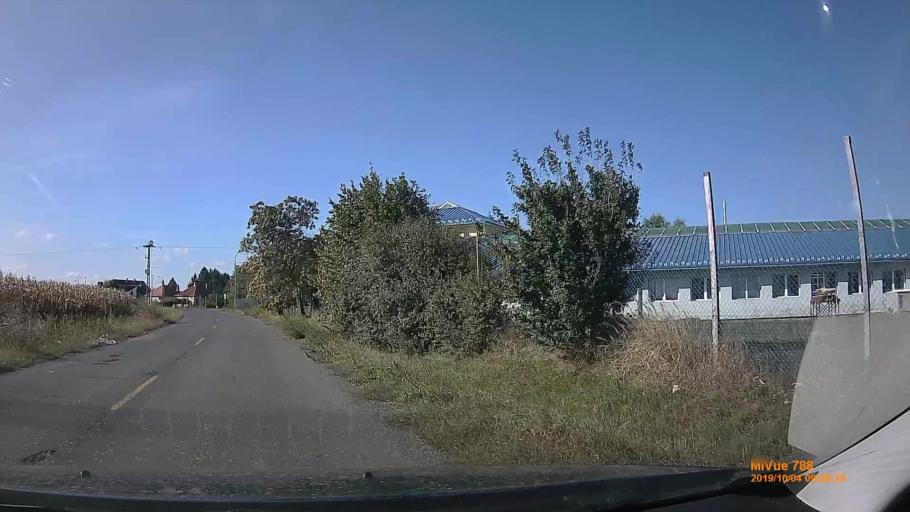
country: HU
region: Somogy
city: Kaposvar
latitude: 46.4240
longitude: 17.7764
